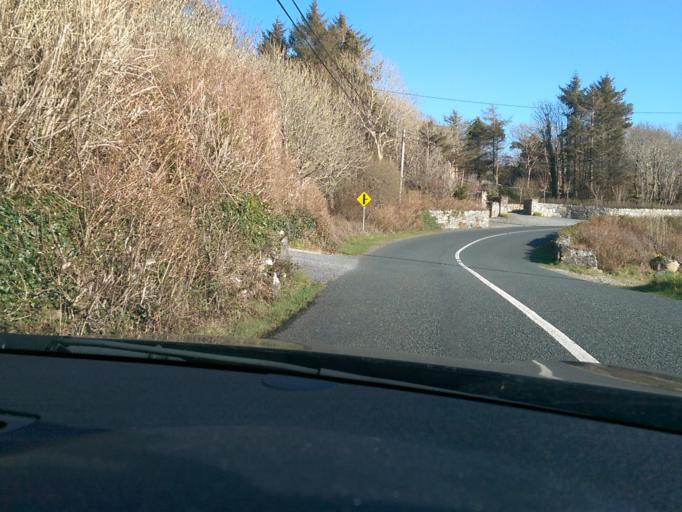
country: IE
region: Connaught
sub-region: County Galway
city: Clifden
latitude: 53.4165
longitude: -9.7973
